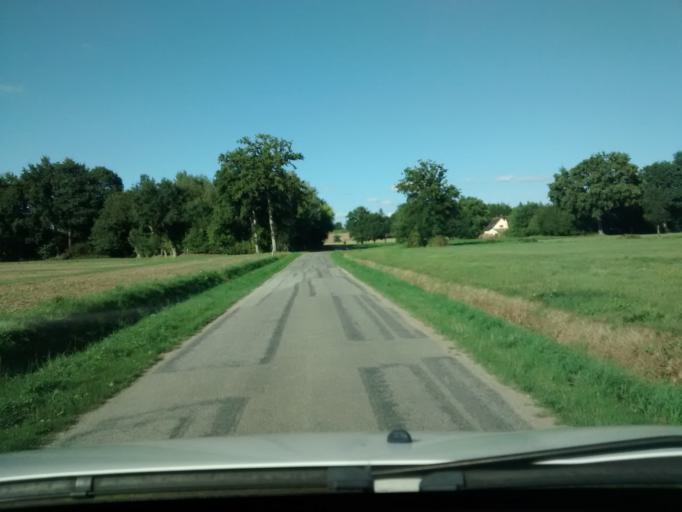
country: FR
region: Brittany
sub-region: Departement d'Ille-et-Vilaine
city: Nouvoitou
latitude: 48.0763
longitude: -1.5623
